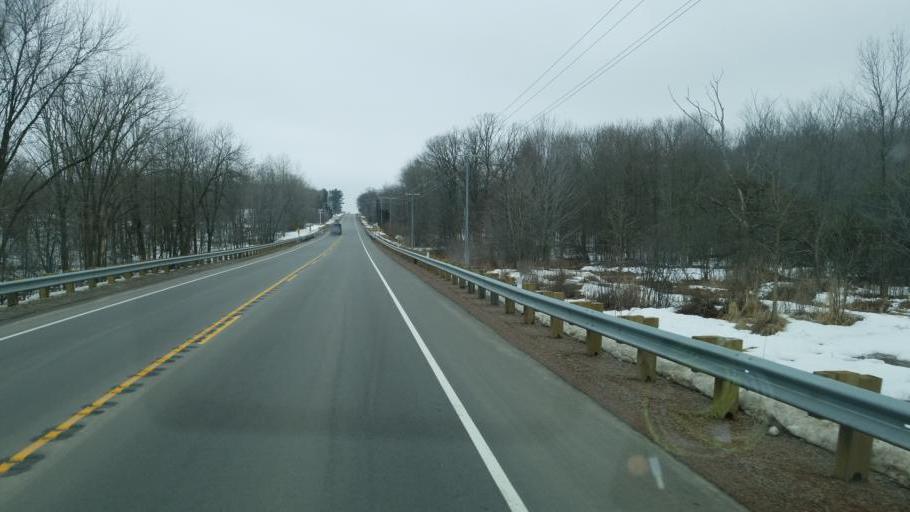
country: US
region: Wisconsin
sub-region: Wood County
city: Marshfield
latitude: 44.6564
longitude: -90.2521
